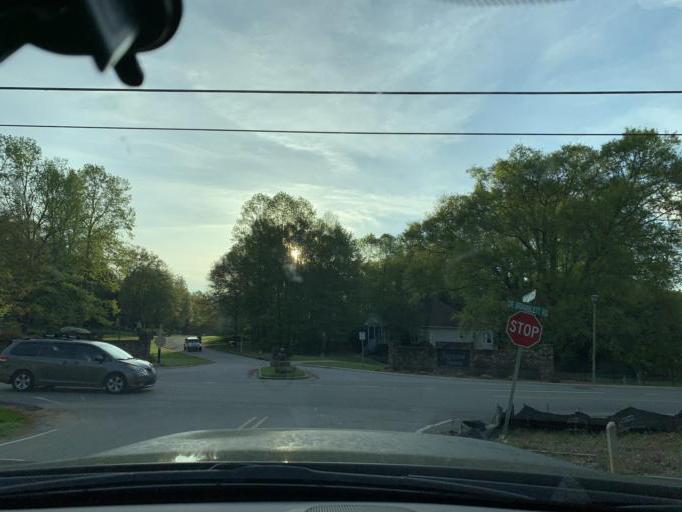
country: US
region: Georgia
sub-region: Forsyth County
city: Cumming
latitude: 34.2531
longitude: -84.1704
